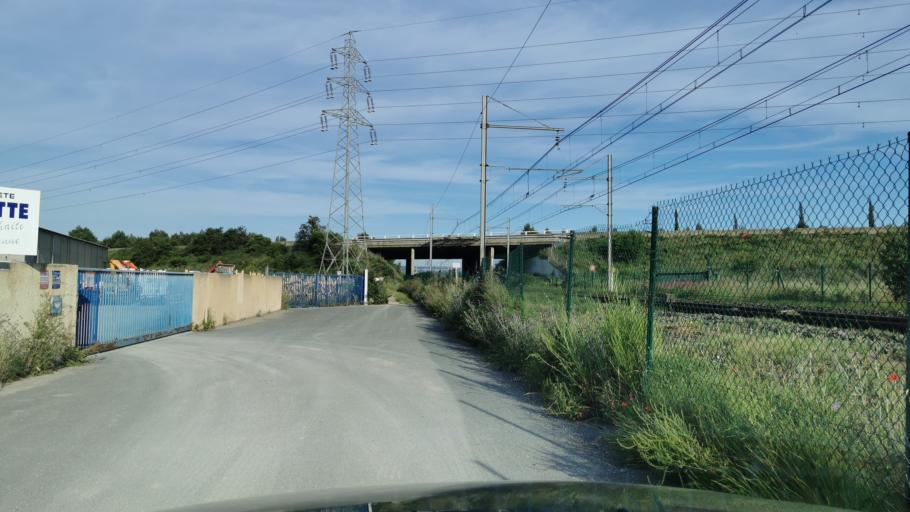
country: FR
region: Languedoc-Roussillon
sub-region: Departement de l'Aude
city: Narbonne
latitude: 43.1666
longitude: 2.9984
